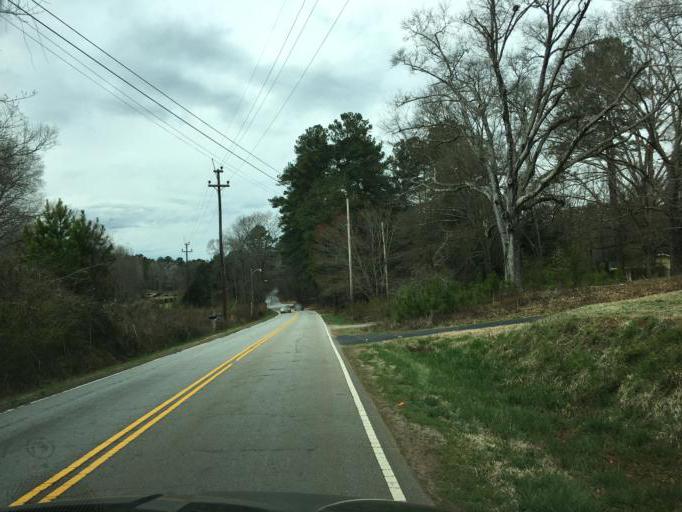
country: US
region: South Carolina
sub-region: Anderson County
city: Pendleton
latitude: 34.6594
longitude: -82.7882
